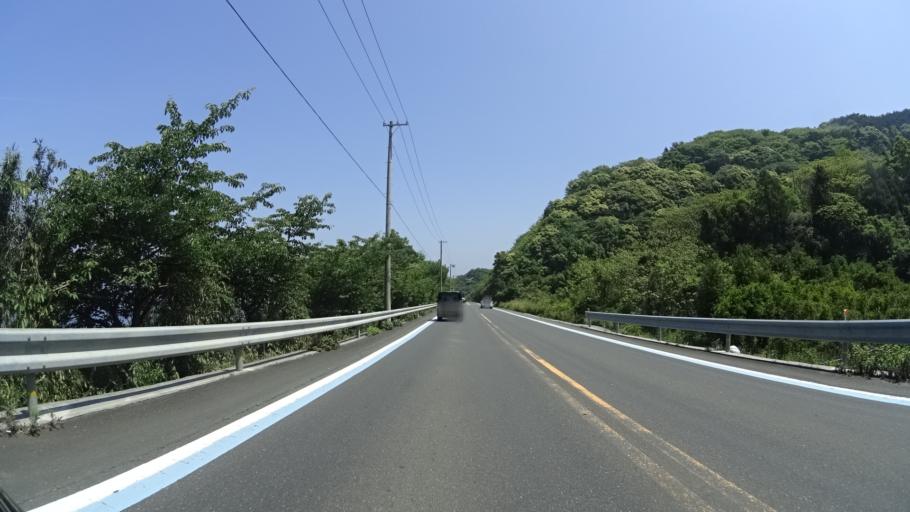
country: JP
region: Ehime
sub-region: Nishiuwa-gun
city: Ikata-cho
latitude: 33.5359
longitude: 132.4003
